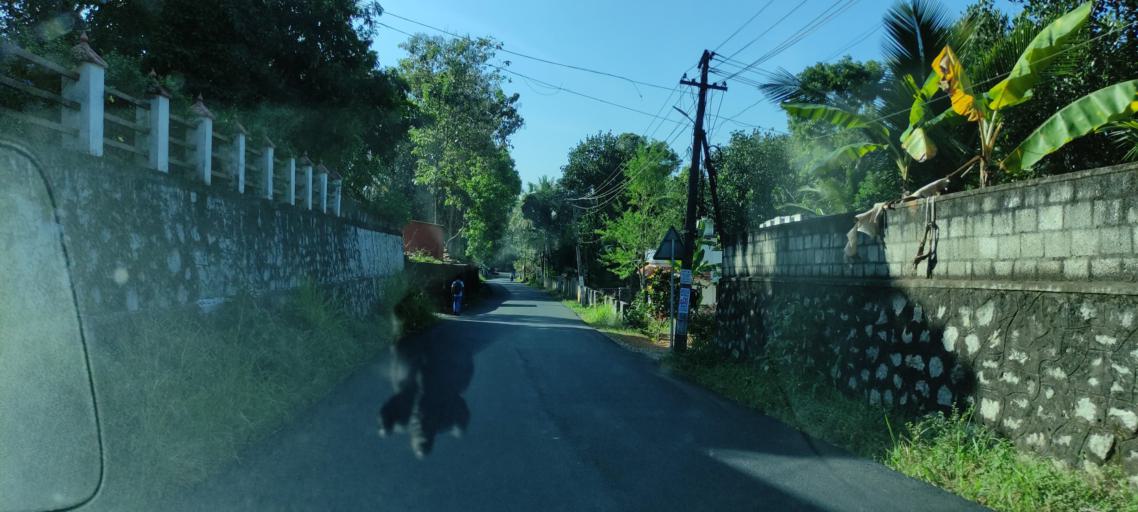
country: IN
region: Kerala
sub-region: Pattanamtitta
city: Adur
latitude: 9.1581
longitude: 76.7151
